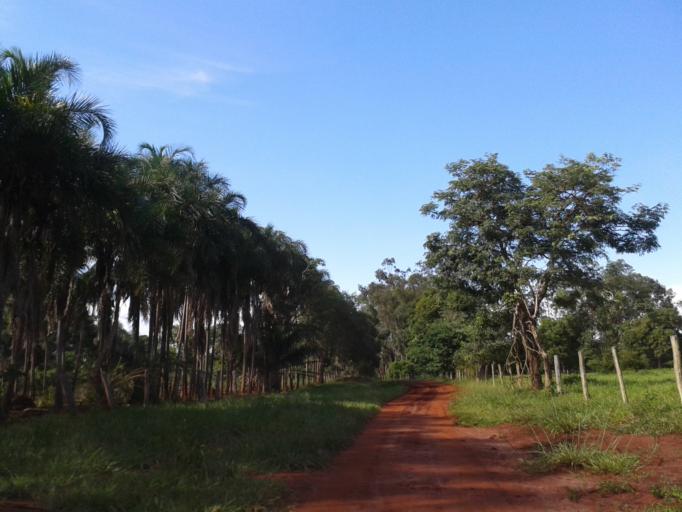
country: BR
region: Minas Gerais
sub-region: Santa Vitoria
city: Santa Vitoria
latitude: -19.1127
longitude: -50.5375
